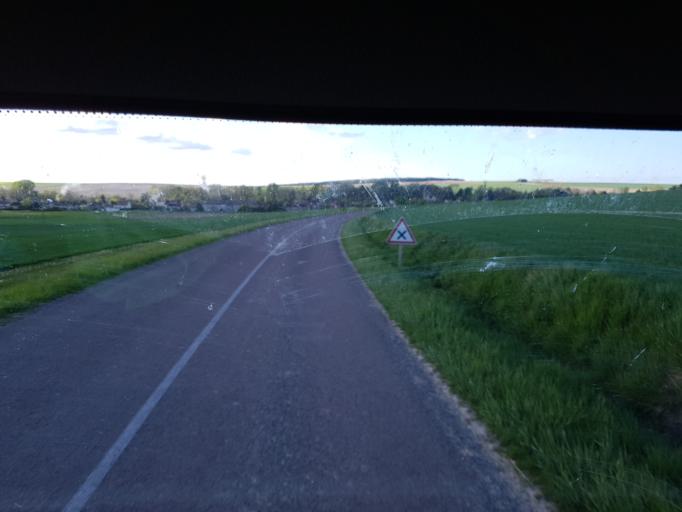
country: FR
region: Champagne-Ardenne
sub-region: Departement de l'Aube
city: Marigny-le-Chatel
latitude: 48.3416
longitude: 3.6346
